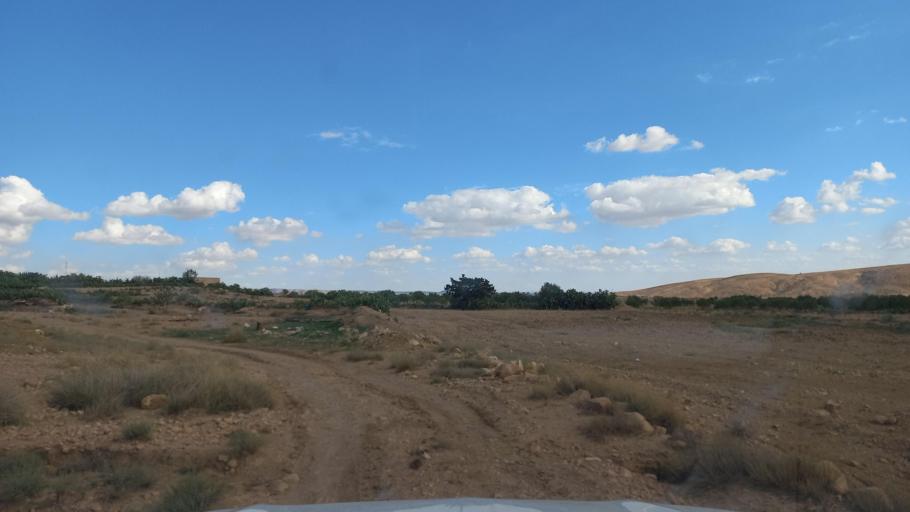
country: TN
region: Al Qasrayn
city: Sbiba
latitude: 35.4027
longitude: 9.0121
